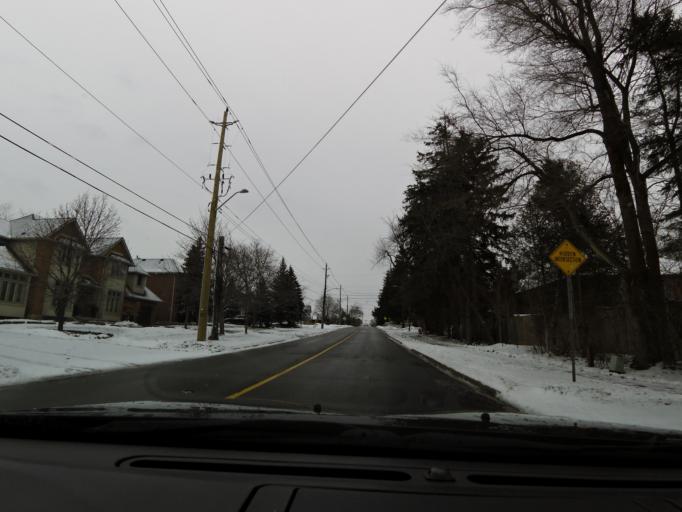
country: CA
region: Ontario
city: Ancaster
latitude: 43.2231
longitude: -79.9676
